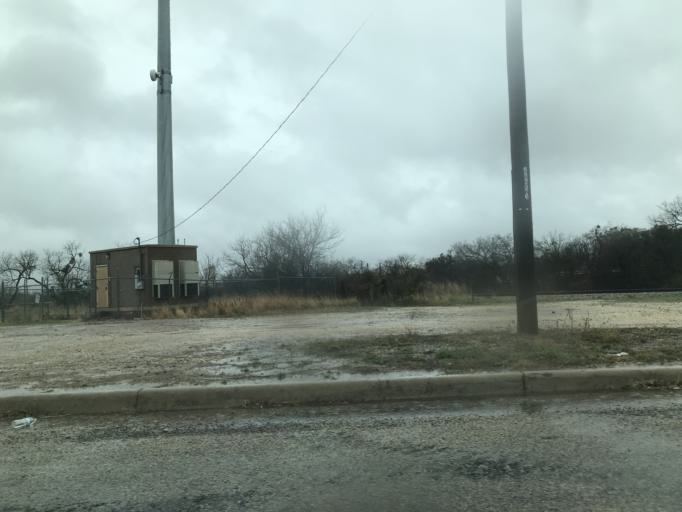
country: US
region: Texas
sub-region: Tom Green County
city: San Angelo
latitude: 31.4641
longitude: -100.4228
